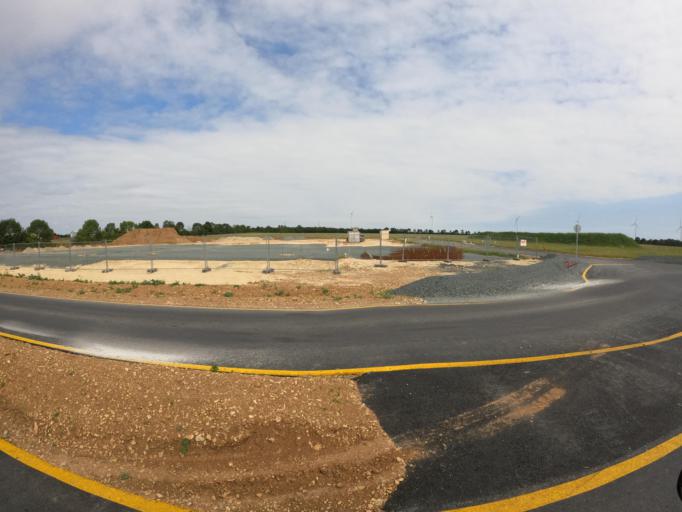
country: FR
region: Poitou-Charentes
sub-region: Departement de la Charente-Maritime
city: Saint-Jean-de-Liversay
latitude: 46.2296
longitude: -0.8777
